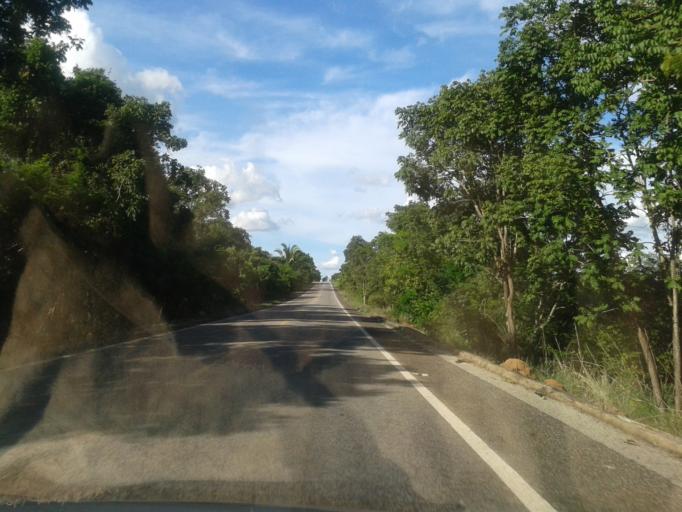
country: BR
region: Goias
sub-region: Mozarlandia
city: Mozarlandia
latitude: -14.5397
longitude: -50.4893
